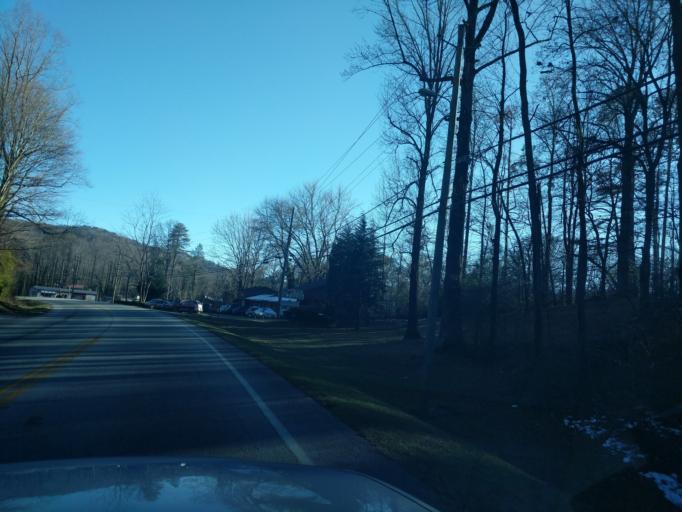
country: US
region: Georgia
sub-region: Rabun County
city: Clayton
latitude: 34.8670
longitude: -83.3982
